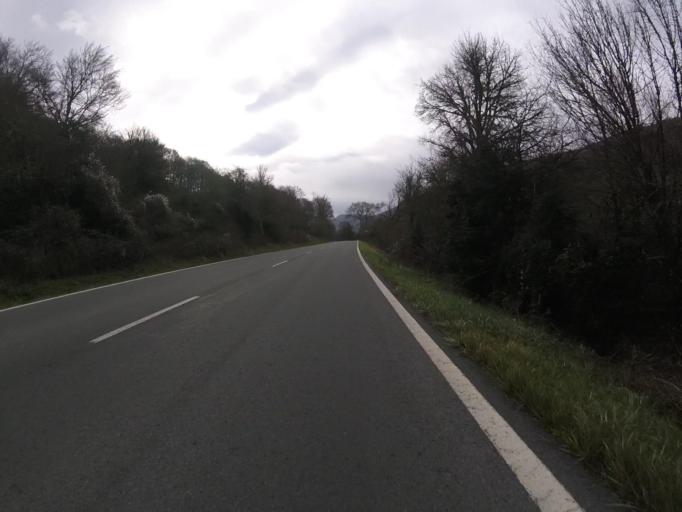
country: ES
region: Navarre
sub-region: Provincia de Navarra
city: Lezaun
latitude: 42.8298
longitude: -2.0279
